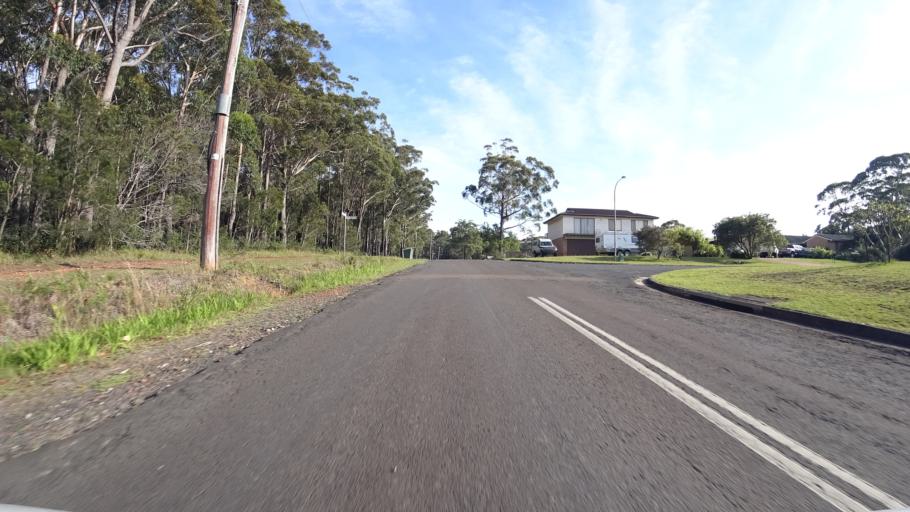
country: AU
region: New South Wales
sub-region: Shoalhaven Shire
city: Milton
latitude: -35.2592
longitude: 150.5052
